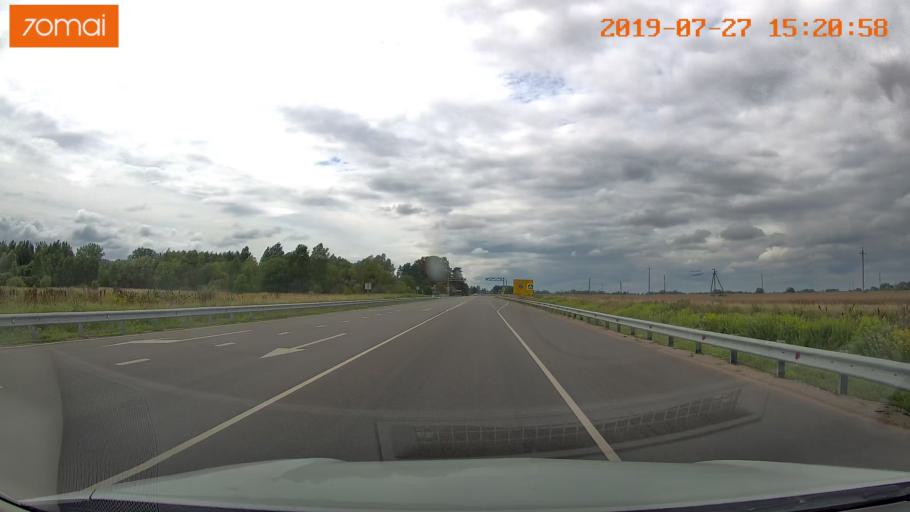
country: LT
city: Kybartai
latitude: 54.6336
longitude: 22.6929
